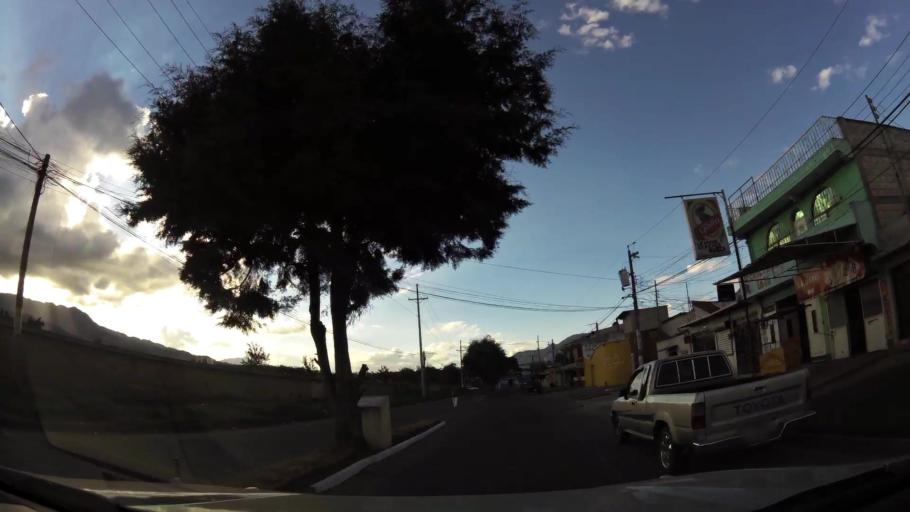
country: GT
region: Quetzaltenango
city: Quetzaltenango
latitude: 14.8517
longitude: -91.5287
